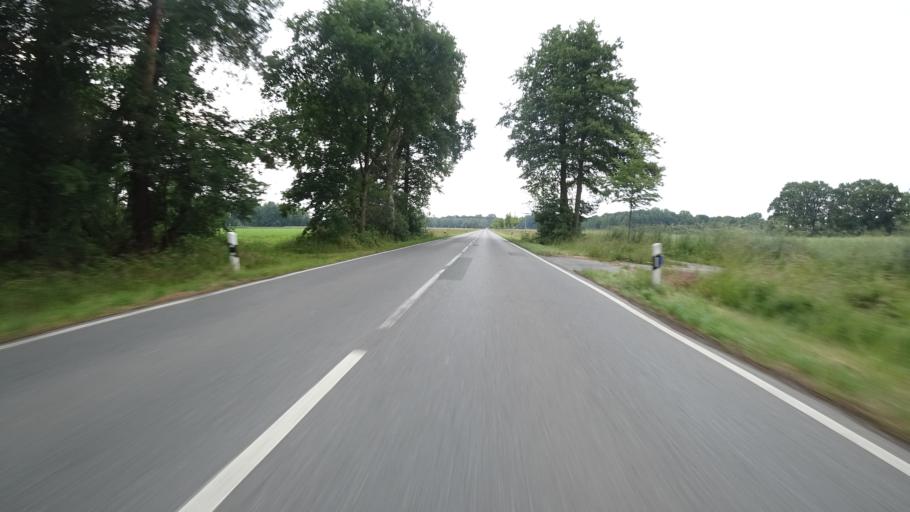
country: DE
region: North Rhine-Westphalia
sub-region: Regierungsbezirk Detmold
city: Guetersloh
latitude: 51.9355
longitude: 8.3799
